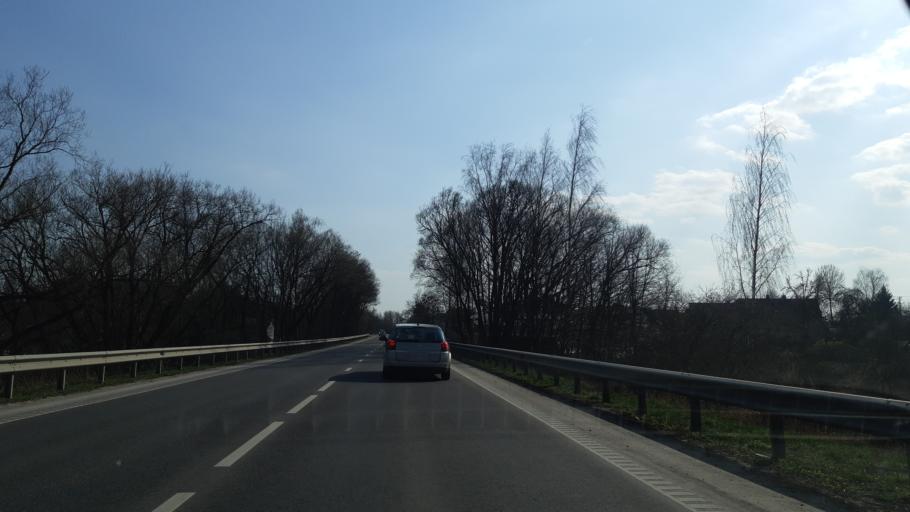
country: LT
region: Kauno apskritis
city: Dainava (Kaunas)
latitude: 54.8659
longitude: 23.9866
